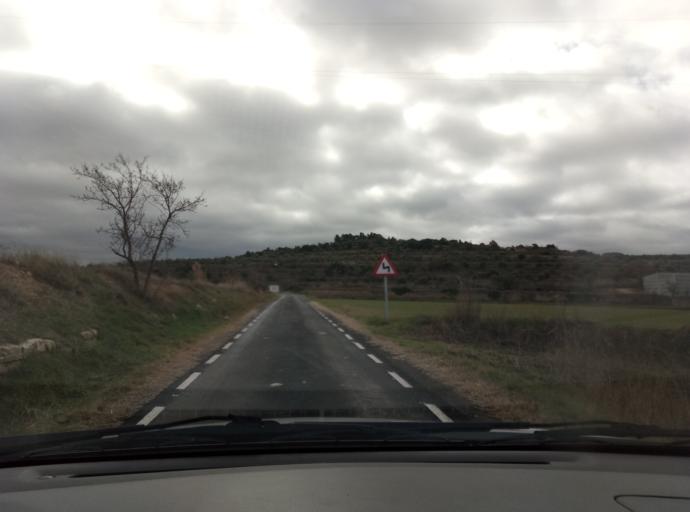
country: ES
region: Catalonia
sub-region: Provincia de Lleida
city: Vallbona de les Monges
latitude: 41.5581
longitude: 1.0657
